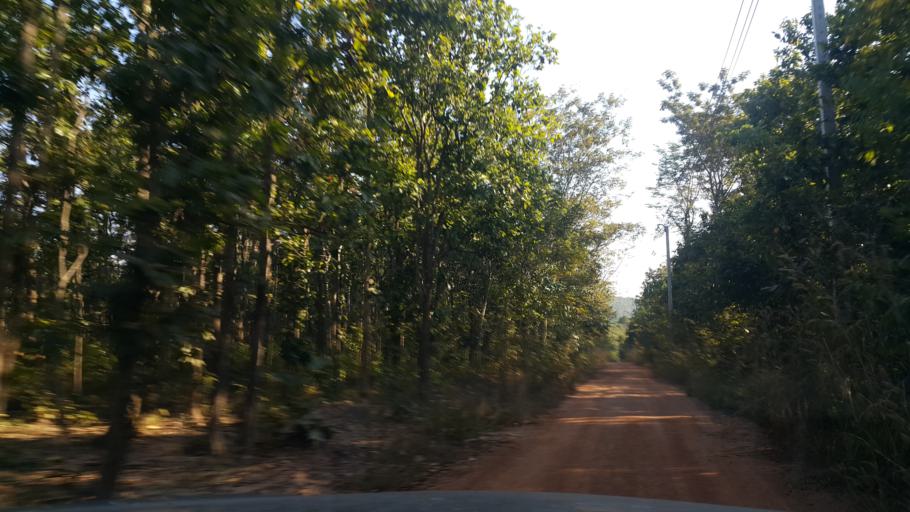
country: TH
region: Lamphun
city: Mae Tha
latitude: 18.5228
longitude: 99.1168
